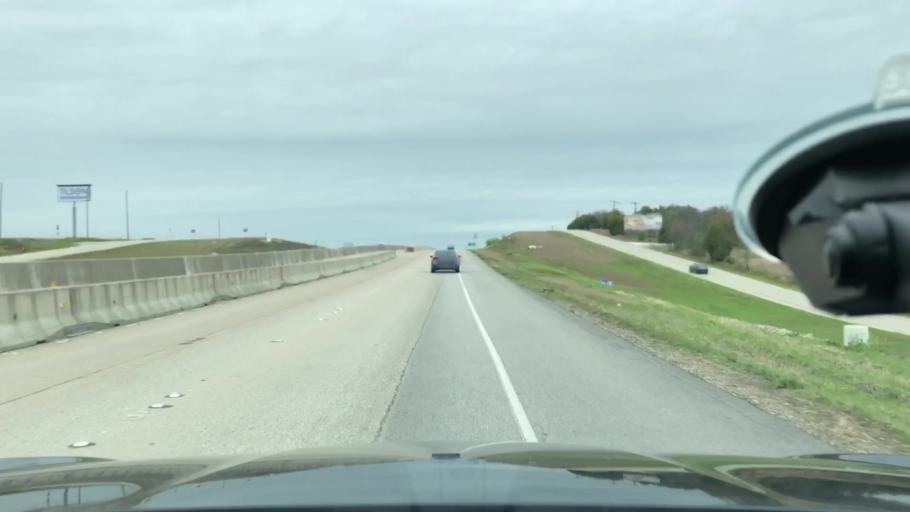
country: US
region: Texas
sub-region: Ellis County
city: Waxahachie
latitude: 32.3814
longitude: -96.8662
